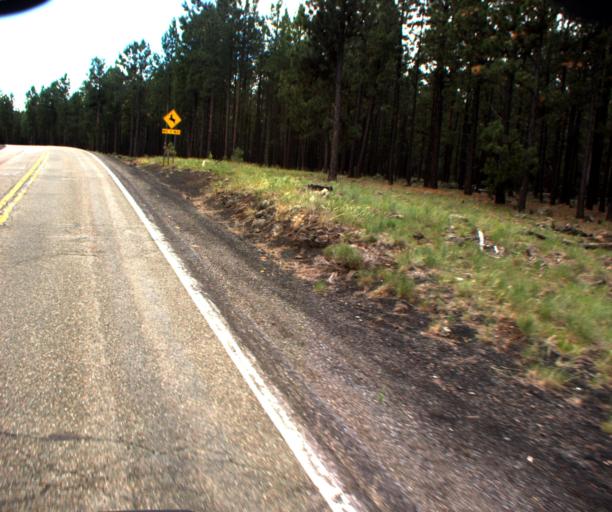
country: US
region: Arizona
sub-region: Coconino County
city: Parks
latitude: 35.3538
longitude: -111.7911
